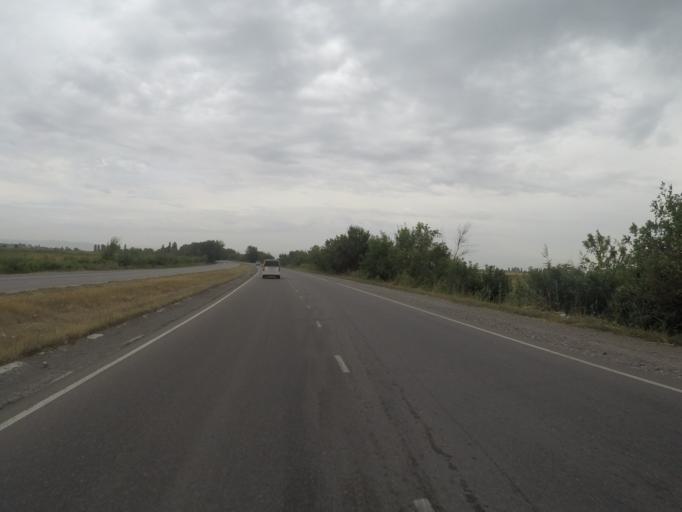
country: KG
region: Chuy
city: Lebedinovka
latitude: 42.9240
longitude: 74.7606
